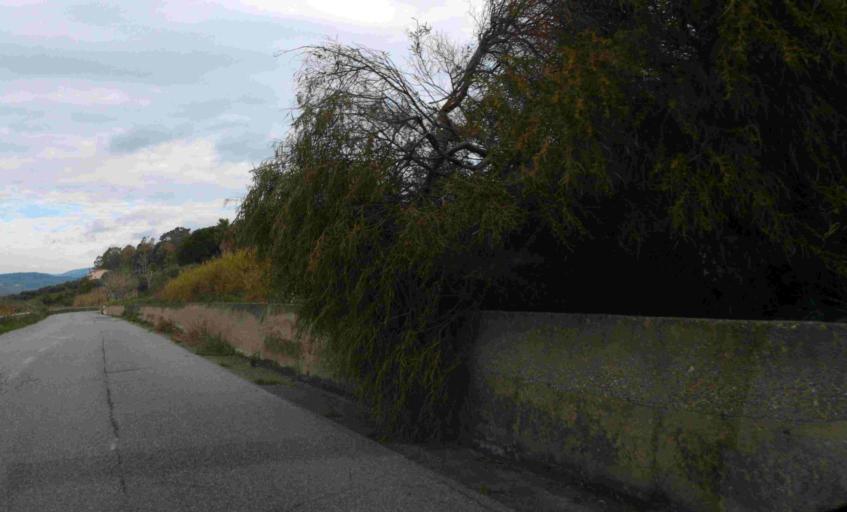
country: IT
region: Calabria
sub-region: Provincia di Catanzaro
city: Sellia Marina
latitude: 38.8861
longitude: 16.7111
